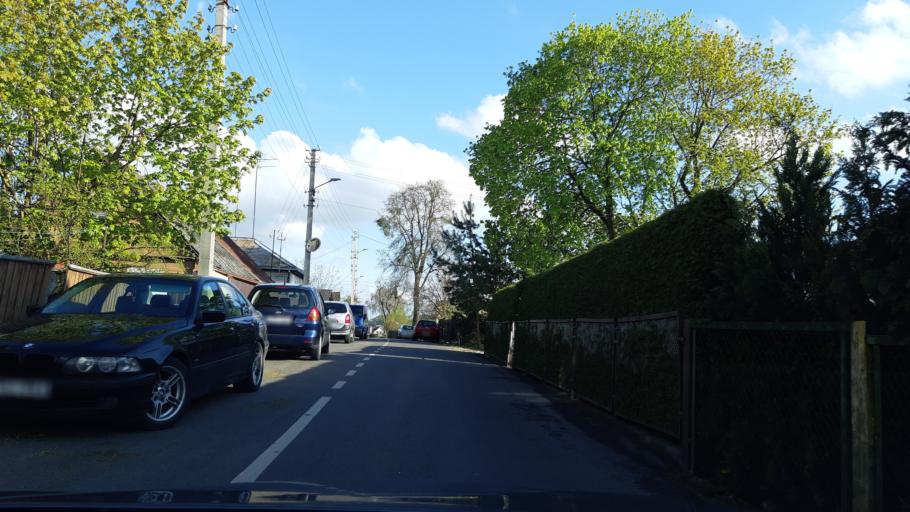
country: LT
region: Kauno apskritis
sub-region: Kaunas
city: Aleksotas
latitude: 54.8661
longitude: 23.9325
